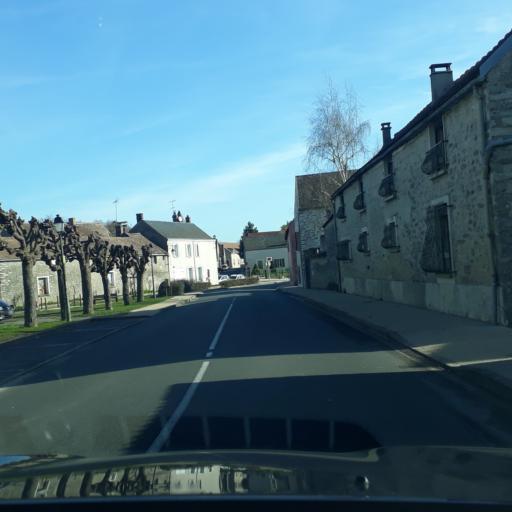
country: FR
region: Ile-de-France
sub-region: Departement de l'Essonne
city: Boissy-le-Cutte
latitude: 48.4548
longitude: 2.2577
